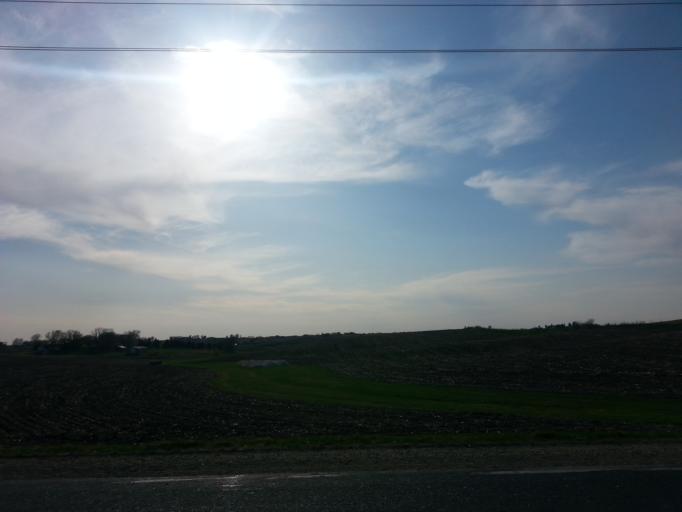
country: US
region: Wisconsin
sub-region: Pierce County
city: Ellsworth
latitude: 44.7235
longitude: -92.6090
